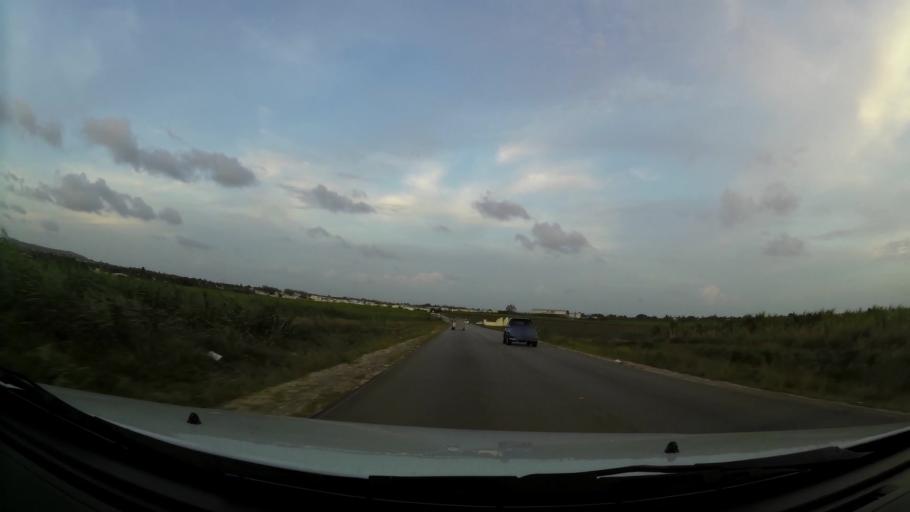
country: BB
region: Saint Philip
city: Crane
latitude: 13.1106
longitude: -59.4835
